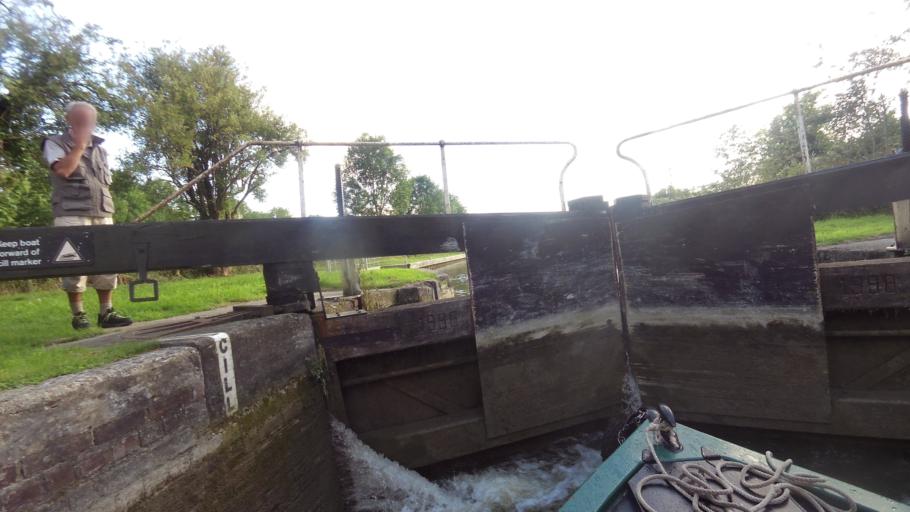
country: GB
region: England
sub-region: Wiltshire
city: Great Bedwyn
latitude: 51.3823
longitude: -1.5943
